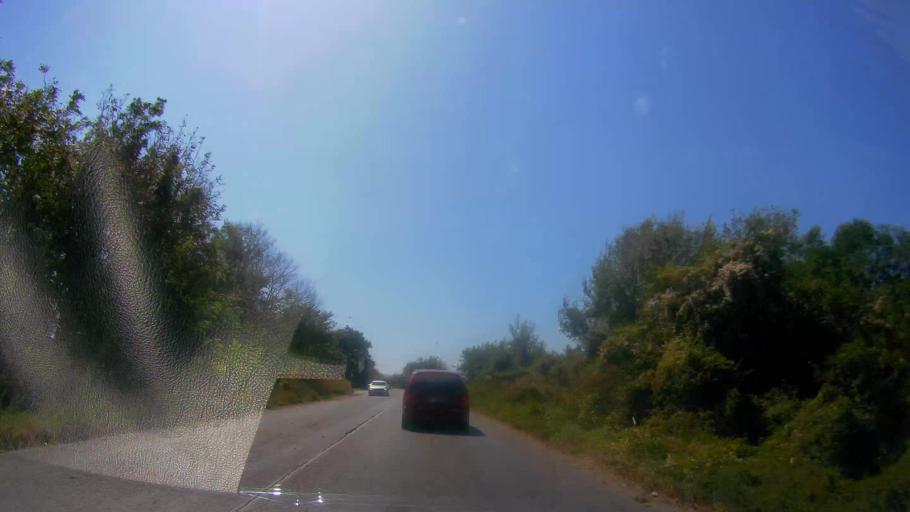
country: BG
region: Veliko Turnovo
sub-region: Obshtina Gorna Oryakhovitsa
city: Purvomaytsi
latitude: 43.2366
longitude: 25.6408
